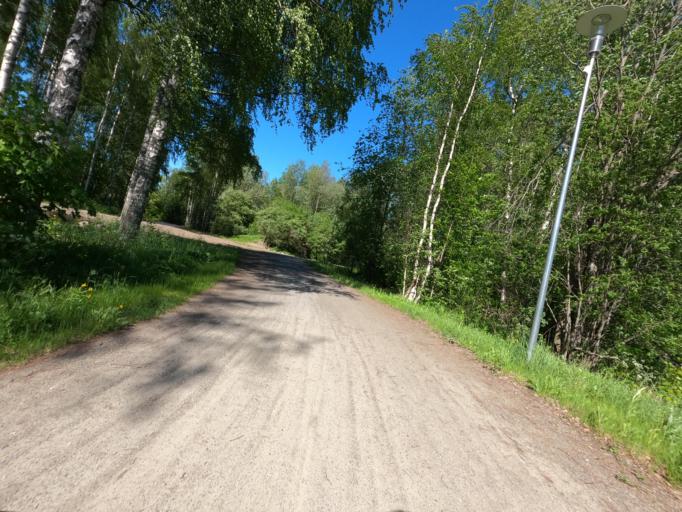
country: FI
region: North Karelia
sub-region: Joensuu
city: Joensuu
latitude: 62.5861
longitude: 29.7579
